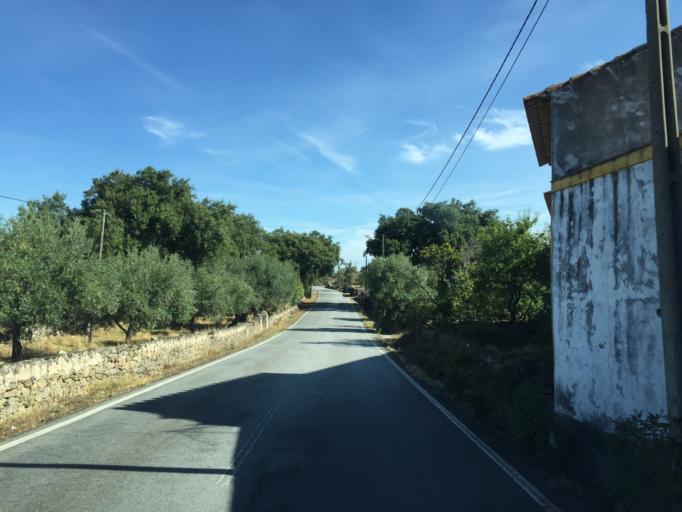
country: PT
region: Portalegre
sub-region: Marvao
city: Marvao
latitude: 39.4040
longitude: -7.3616
